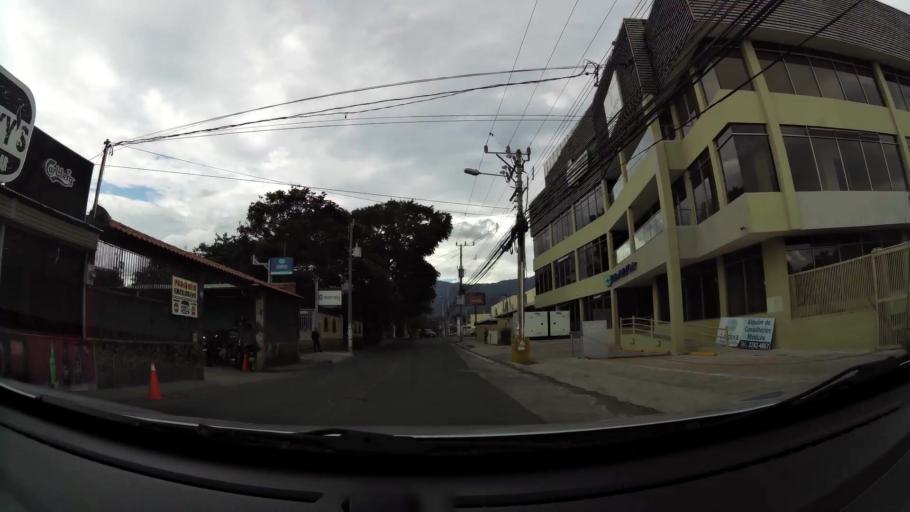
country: CR
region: San Jose
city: Santa Ana
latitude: 9.9536
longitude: -84.1900
